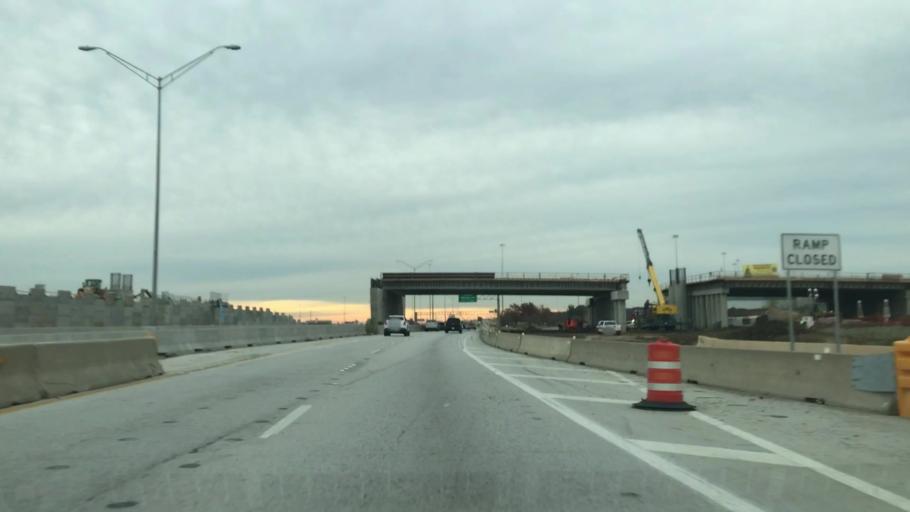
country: US
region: Texas
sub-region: Dallas County
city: Irving
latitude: 32.8437
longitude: -96.9100
